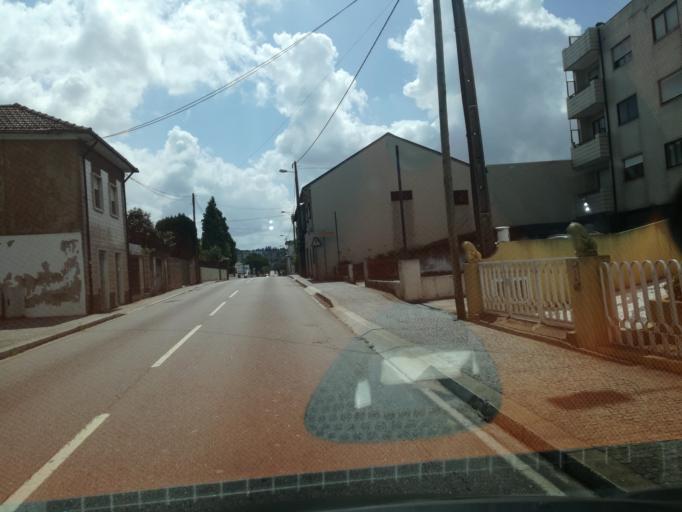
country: PT
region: Porto
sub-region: Maia
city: Nogueira
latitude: 41.2336
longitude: -8.5940
